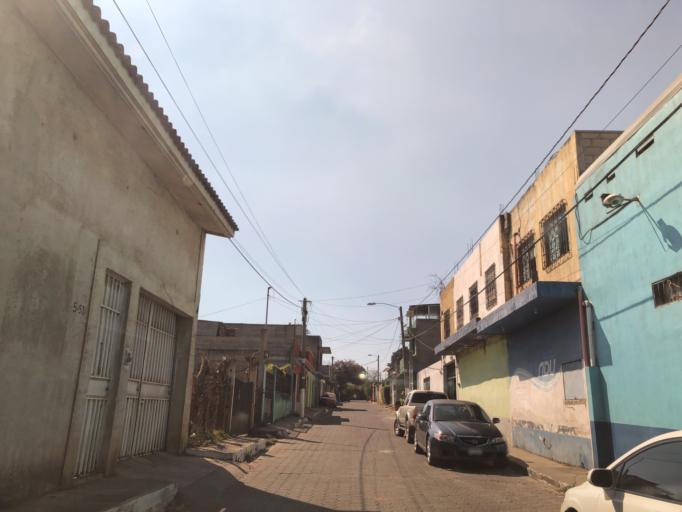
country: GT
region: Guatemala
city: Amatitlan
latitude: 14.5000
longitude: -90.5960
